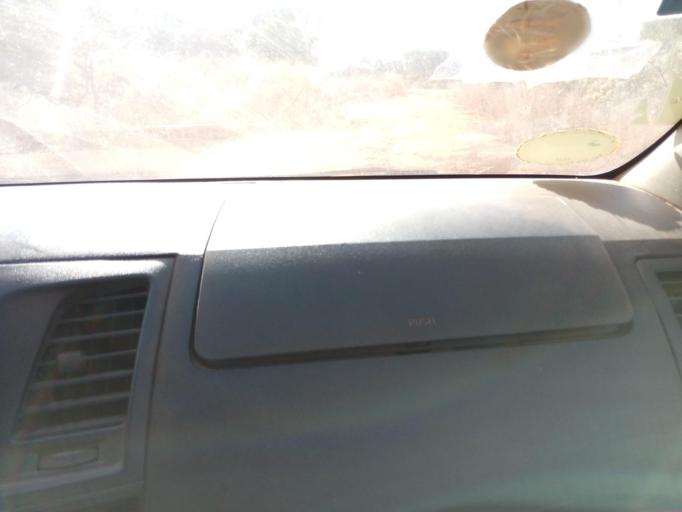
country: ML
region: Sikasso
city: Sikasso
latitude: 11.8763
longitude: -6.0353
